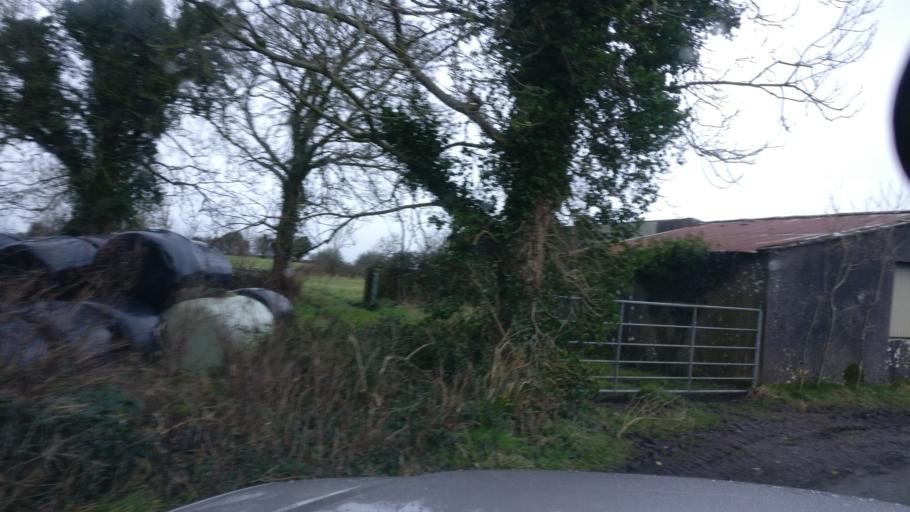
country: IE
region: Connaught
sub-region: County Galway
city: Loughrea
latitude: 53.1908
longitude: -8.6169
